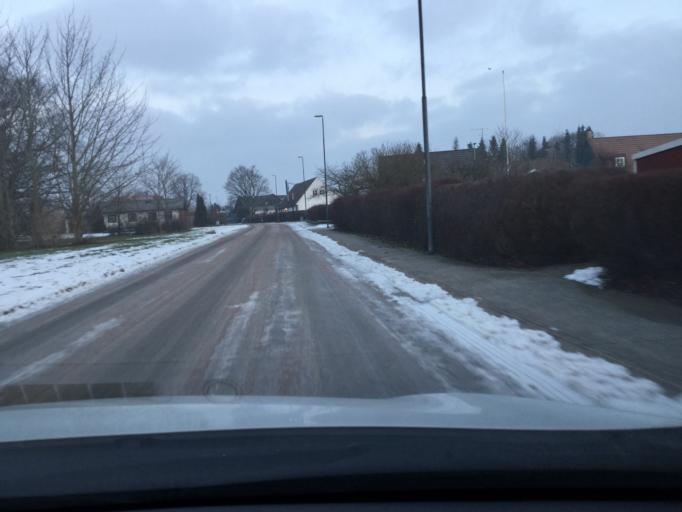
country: SE
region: Skane
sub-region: Hoors Kommun
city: Loberod
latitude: 55.7731
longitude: 13.5119
